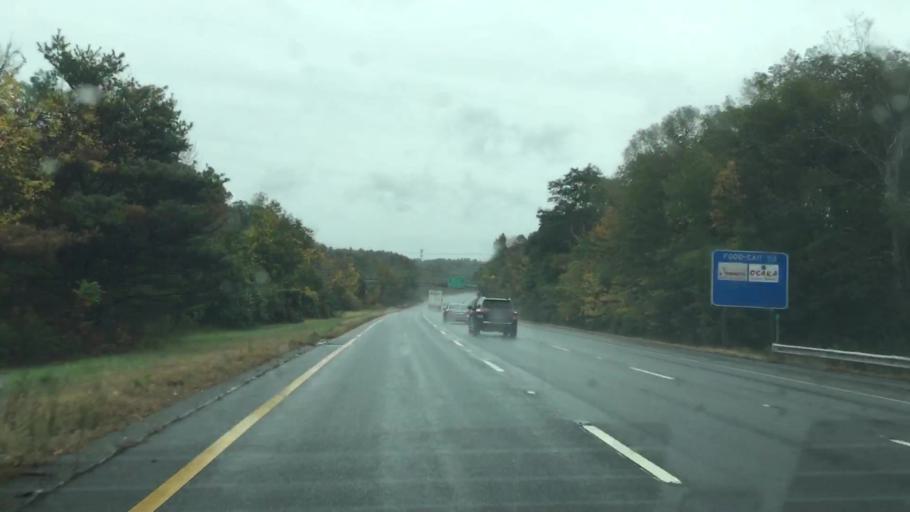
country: US
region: Massachusetts
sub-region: Essex County
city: Merrimac
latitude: 42.8244
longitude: -71.0088
